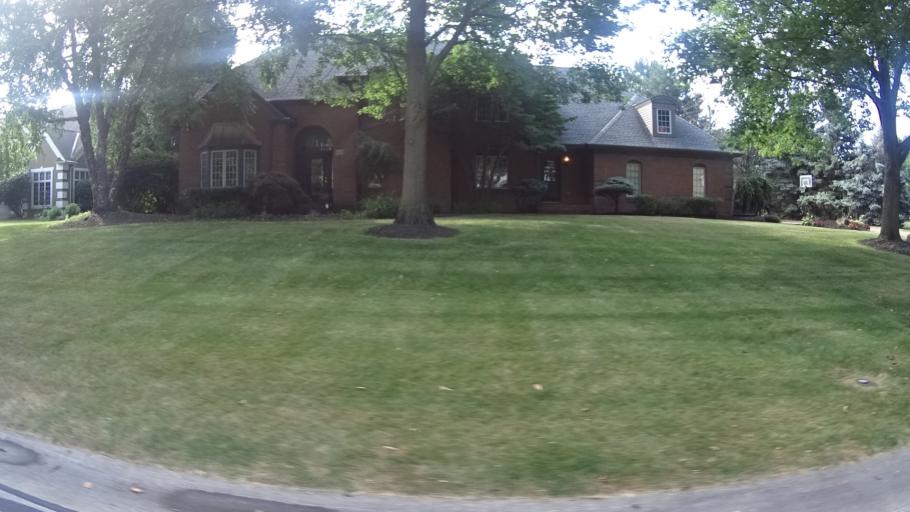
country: US
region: Ohio
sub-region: Erie County
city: Sandusky
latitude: 41.4159
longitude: -82.6598
